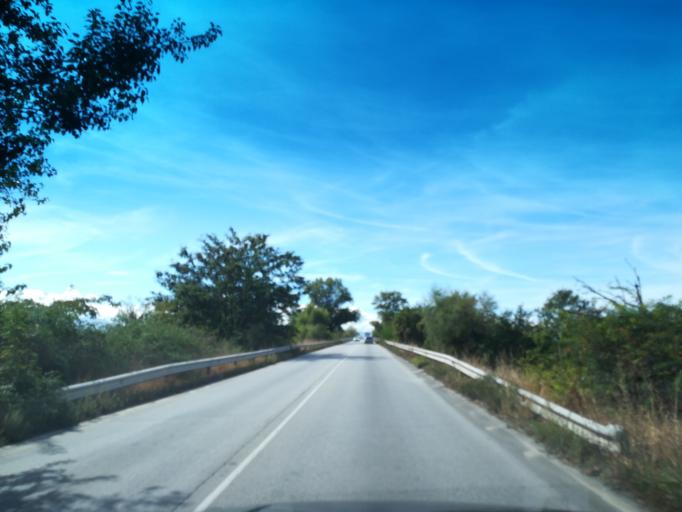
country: BG
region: Plovdiv
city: Stamboliyski
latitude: 42.1326
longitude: 24.6091
